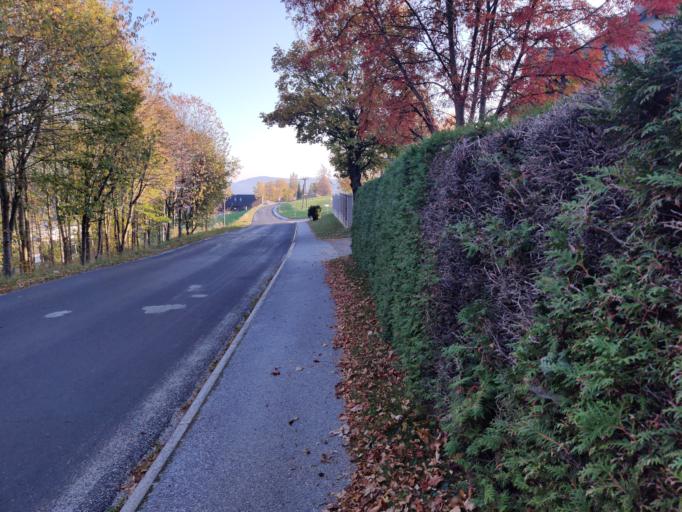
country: AT
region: Styria
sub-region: Politischer Bezirk Hartberg-Fuerstenfeld
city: Sankt Jakob im Walde
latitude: 47.4694
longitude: 15.7855
